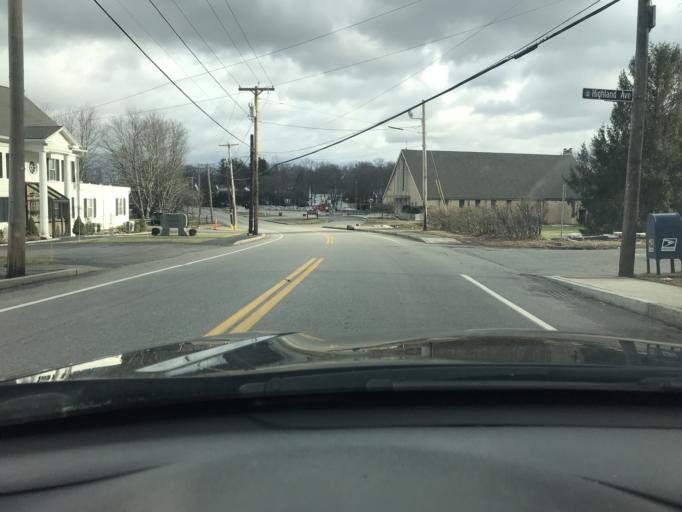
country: US
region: Massachusetts
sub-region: Middlesex County
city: Chelmsford
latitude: 42.6363
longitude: -71.3745
